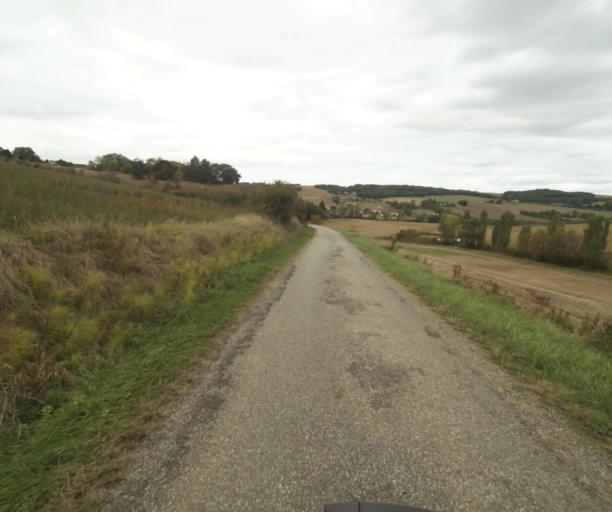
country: FR
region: Midi-Pyrenees
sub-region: Departement du Tarn-et-Garonne
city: Beaumont-de-Lomagne
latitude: 43.8463
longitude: 1.0906
